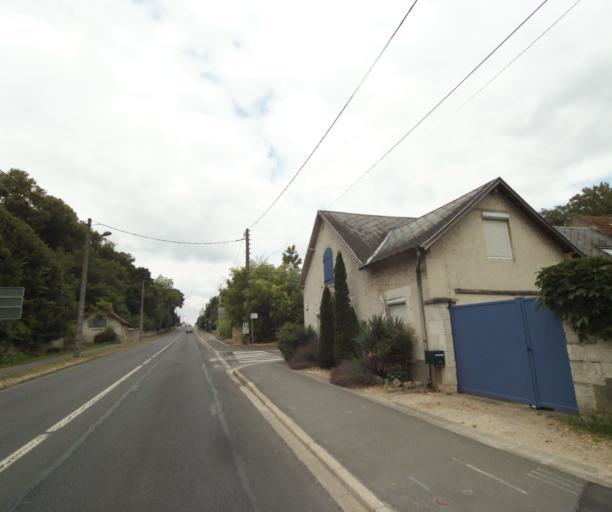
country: FR
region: Centre
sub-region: Departement du Loiret
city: Saint-Jean-de-Braye
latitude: 47.9053
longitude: 1.9892
